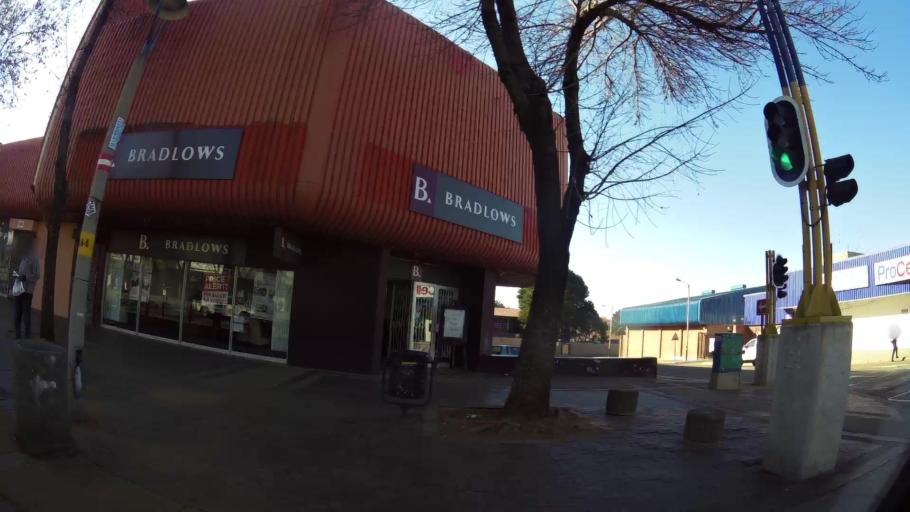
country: ZA
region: Gauteng
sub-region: Ekurhuleni Metropolitan Municipality
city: Germiston
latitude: -26.2675
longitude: 28.1222
